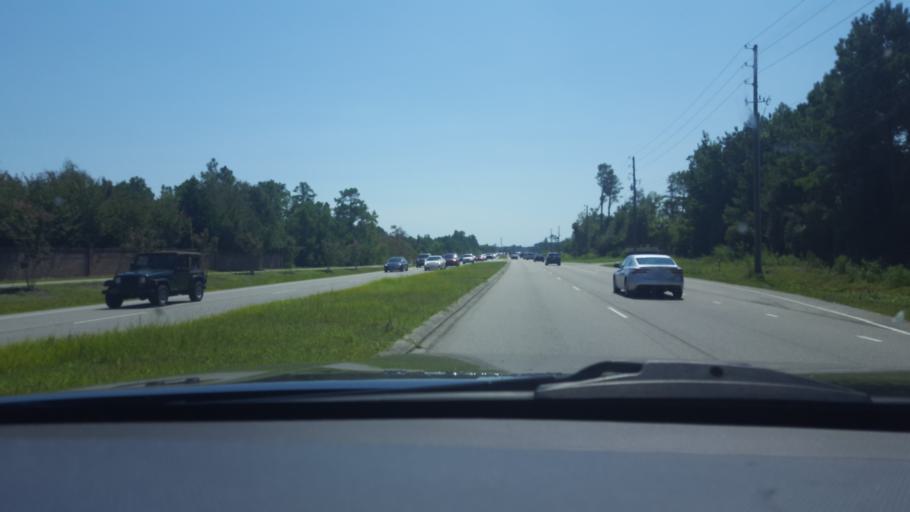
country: US
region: North Carolina
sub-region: New Hanover County
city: Ogden
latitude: 34.2474
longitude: -77.8273
